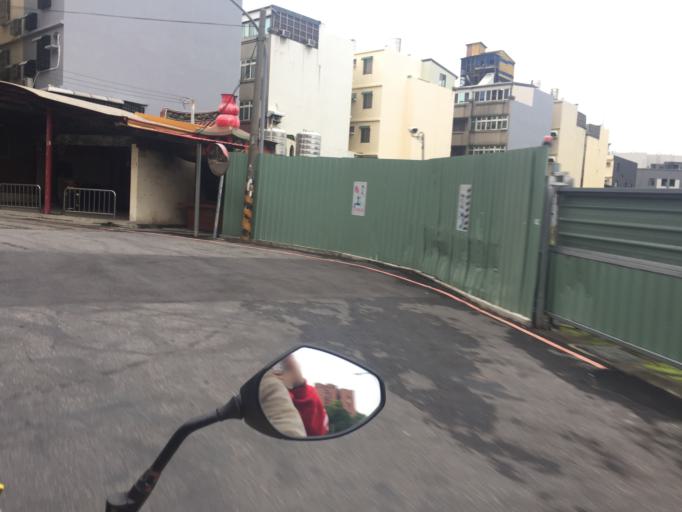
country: TW
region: Taiwan
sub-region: Hsinchu
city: Hsinchu
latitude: 24.7958
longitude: 120.9582
